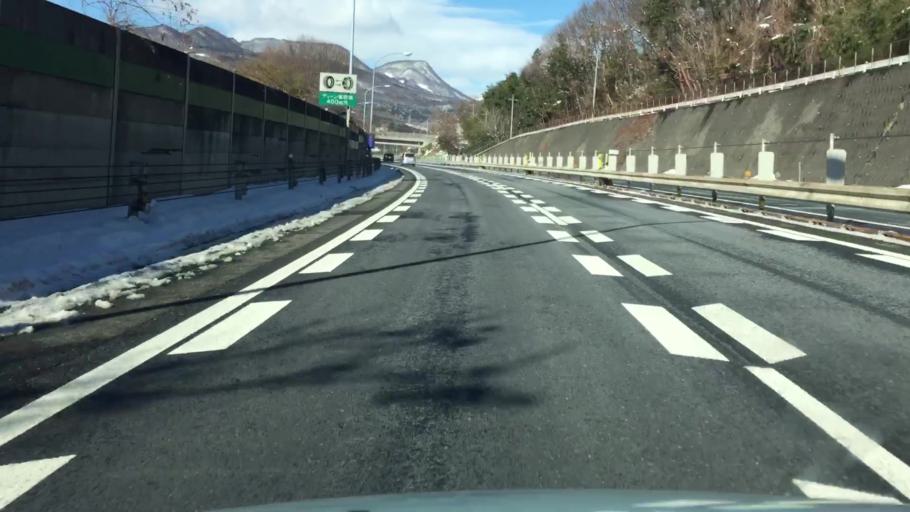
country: JP
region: Gunma
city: Numata
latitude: 36.6983
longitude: 138.9904
